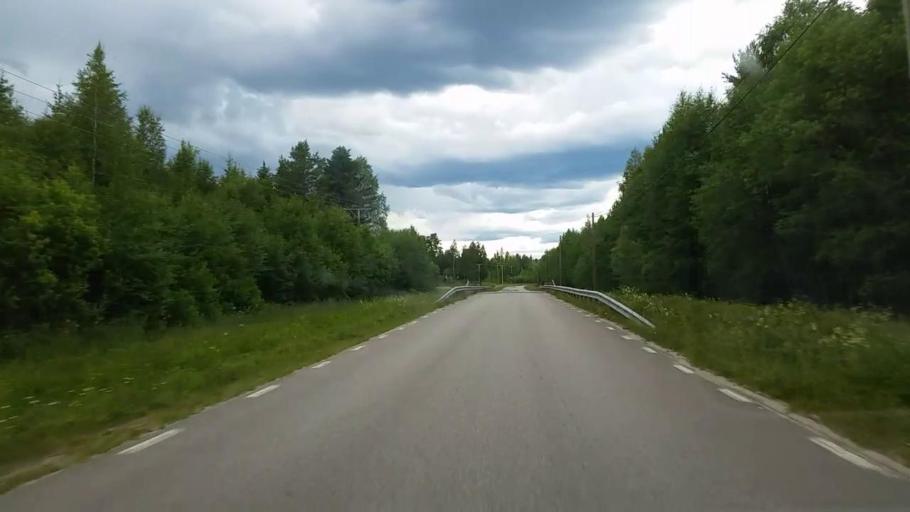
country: SE
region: Gaevleborg
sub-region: Ovanakers Kommun
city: Edsbyn
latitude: 61.4550
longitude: 15.8773
